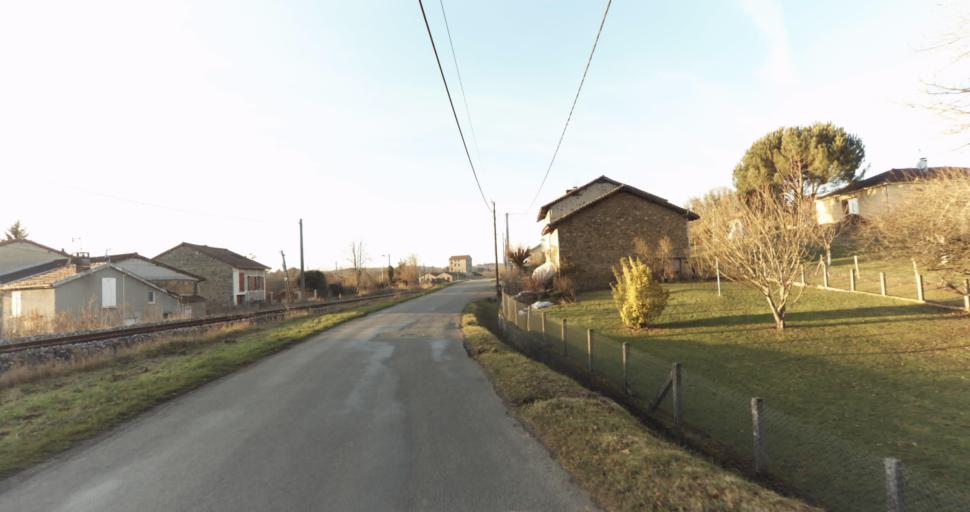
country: FR
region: Limousin
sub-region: Departement de la Haute-Vienne
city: Aixe-sur-Vienne
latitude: 45.8016
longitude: 1.1272
